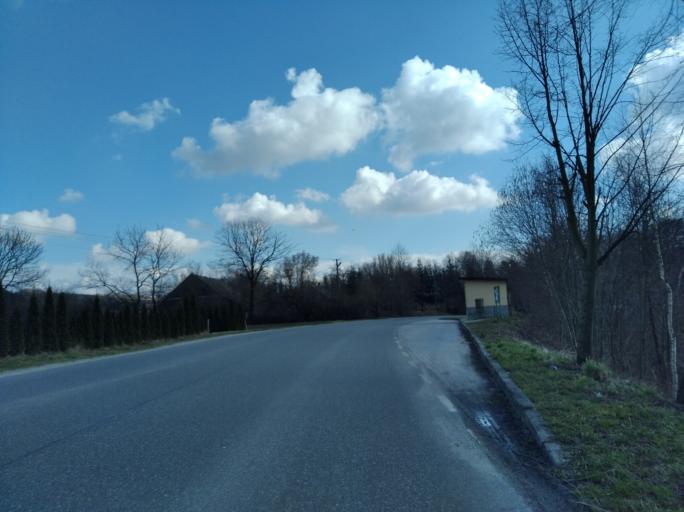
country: PL
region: Subcarpathian Voivodeship
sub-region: Powiat jasielski
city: Kolaczyce
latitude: 49.8586
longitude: 21.4853
